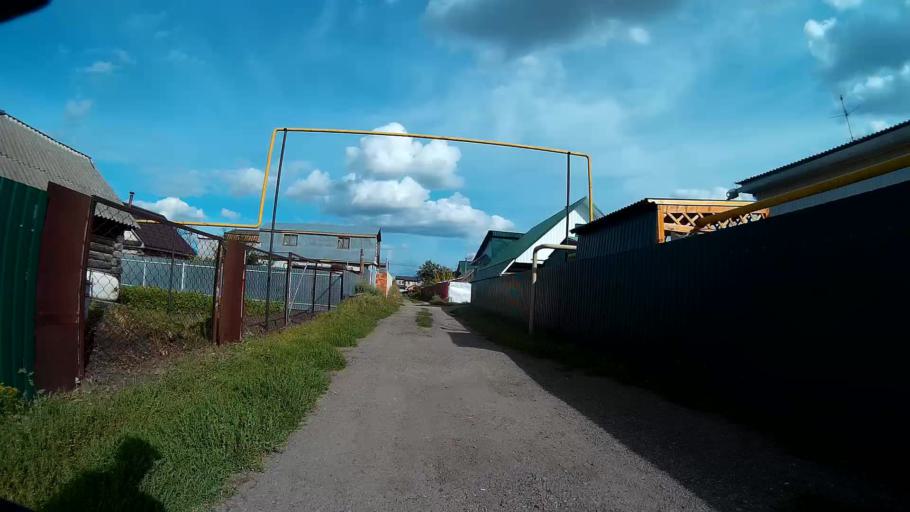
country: RU
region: Ulyanovsk
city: Isheyevka
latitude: 54.2882
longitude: 48.2131
